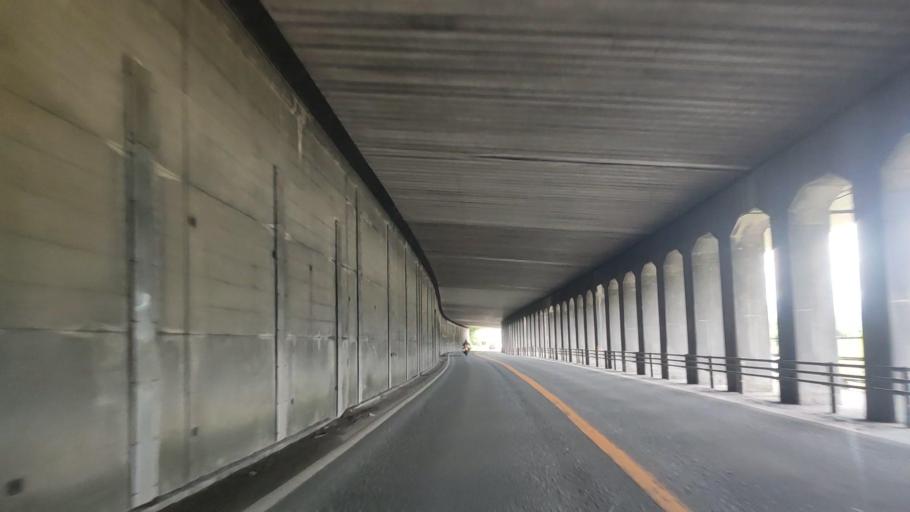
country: JP
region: Gifu
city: Takayama
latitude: 36.1762
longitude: 137.2492
